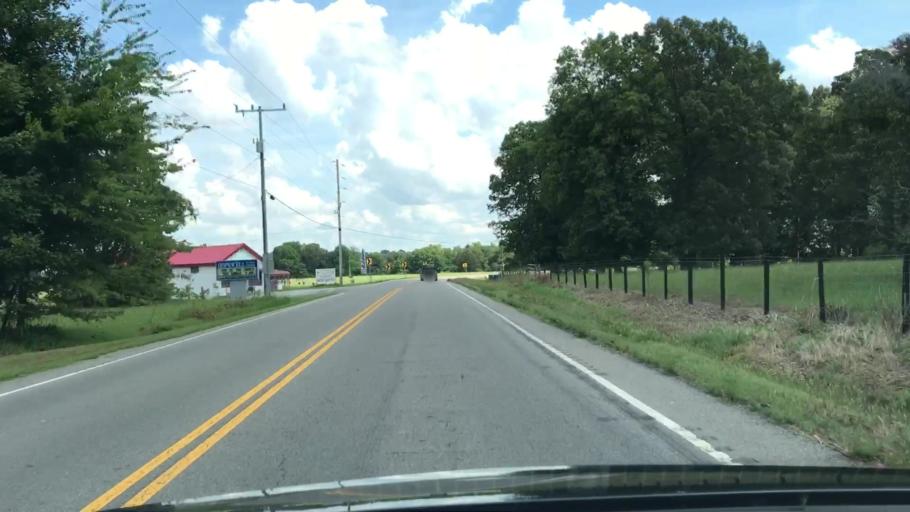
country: US
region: Tennessee
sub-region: Robertson County
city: Springfield
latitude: 36.5544
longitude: -86.8105
